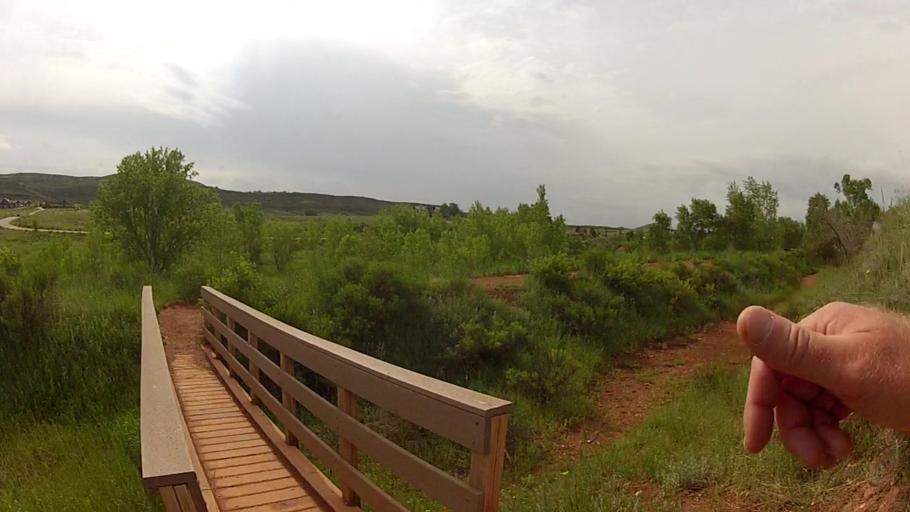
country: US
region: Colorado
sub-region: Larimer County
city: Loveland
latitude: 40.4146
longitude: -105.1533
